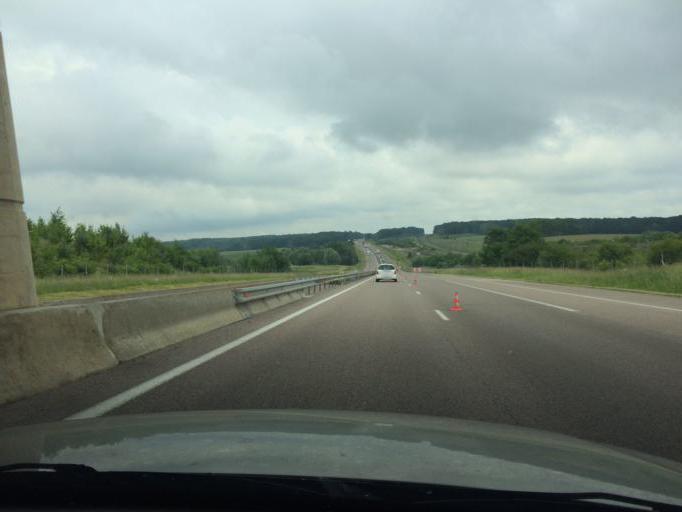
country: FR
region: Picardie
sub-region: Departement de l'Aisne
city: Brasles
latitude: 49.0956
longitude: 3.4368
